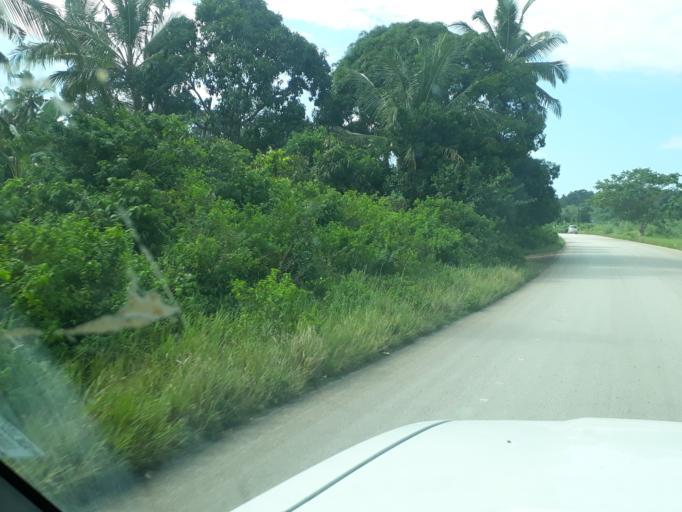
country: TZ
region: Zanzibar North
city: Kijini
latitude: -5.8352
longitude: 39.2897
